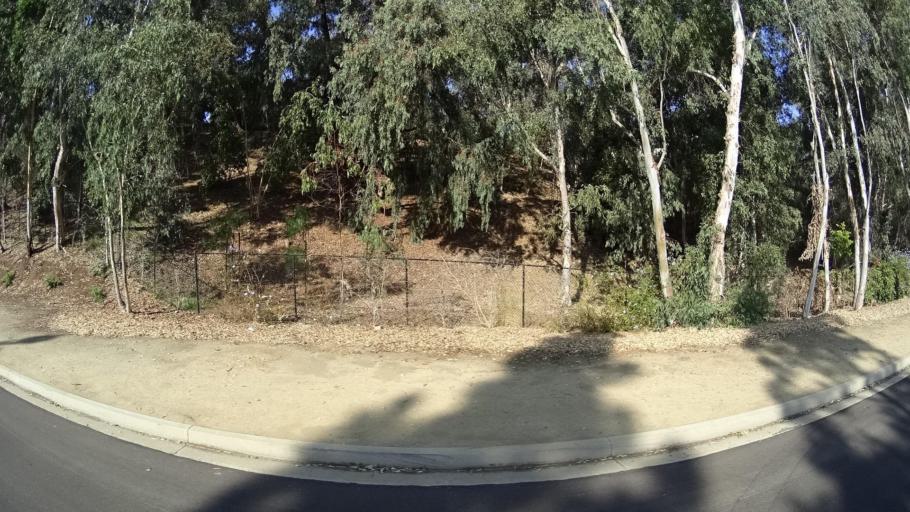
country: US
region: California
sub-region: San Diego County
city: Vista
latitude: 33.1738
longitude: -117.2266
